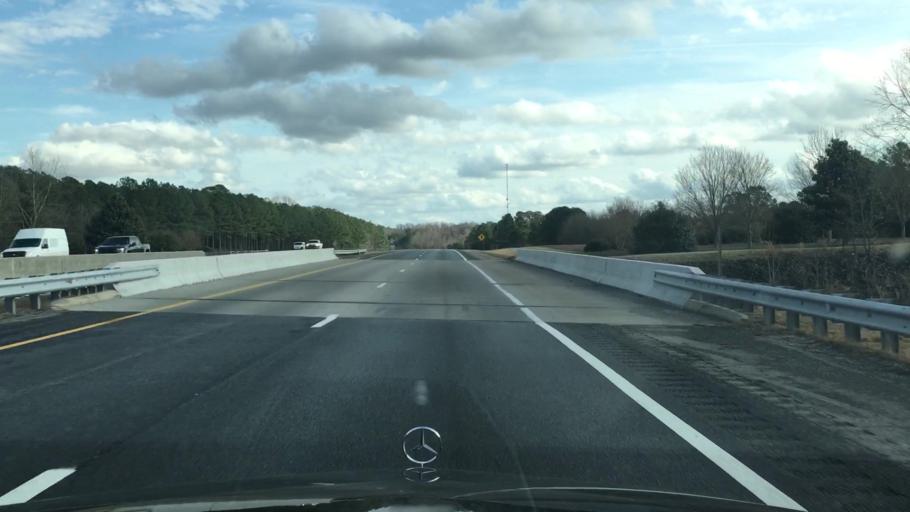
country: US
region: North Carolina
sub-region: Johnston County
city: Benson
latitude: 35.3296
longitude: -78.4493
